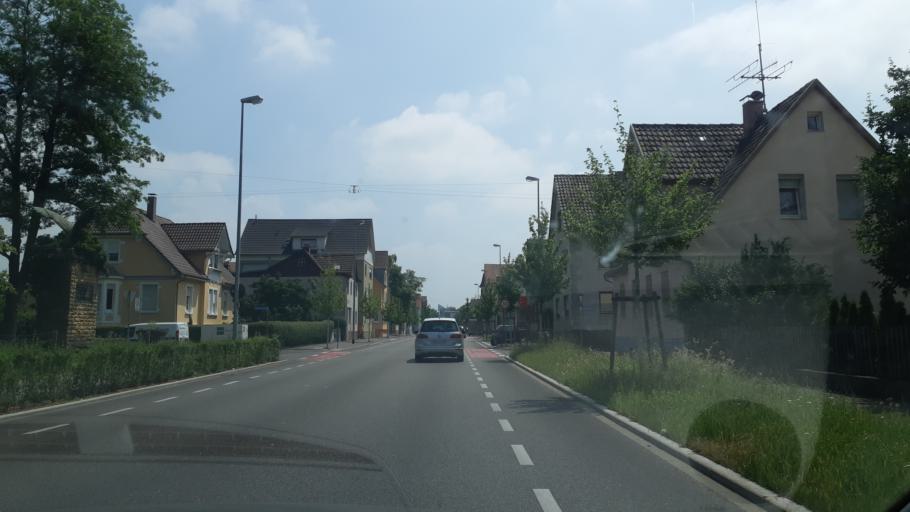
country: DE
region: Baden-Wuerttemberg
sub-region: Regierungsbezirk Stuttgart
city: Eislingen
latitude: 48.6954
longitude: 9.6979
